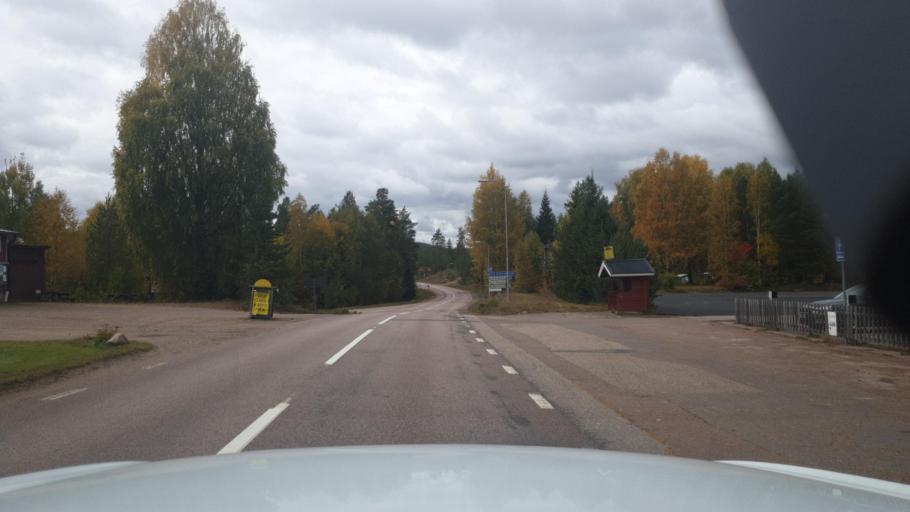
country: SE
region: Vaermland
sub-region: Torsby Kommun
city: Torsby
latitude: 60.1904
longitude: 12.6743
